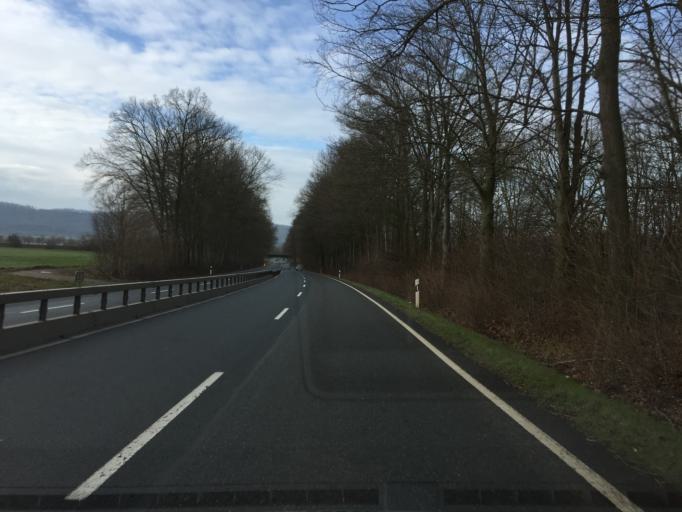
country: DE
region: Lower Saxony
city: Springe
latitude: 52.2162
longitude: 9.5981
